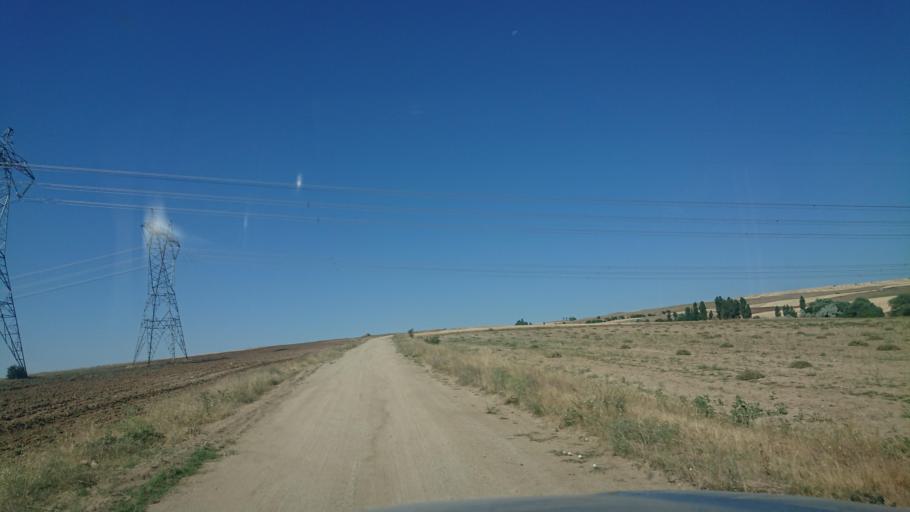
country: TR
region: Aksaray
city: Sariyahsi
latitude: 38.9395
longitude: 33.8695
